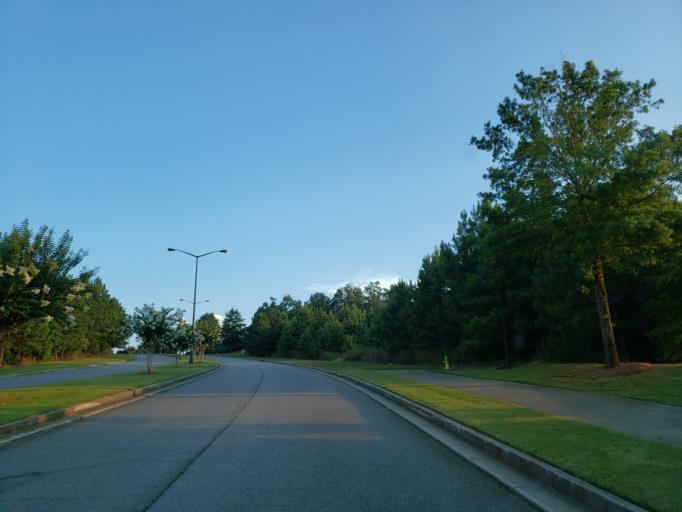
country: US
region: Georgia
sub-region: Bartow County
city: Cartersville
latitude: 34.1142
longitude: -84.8219
